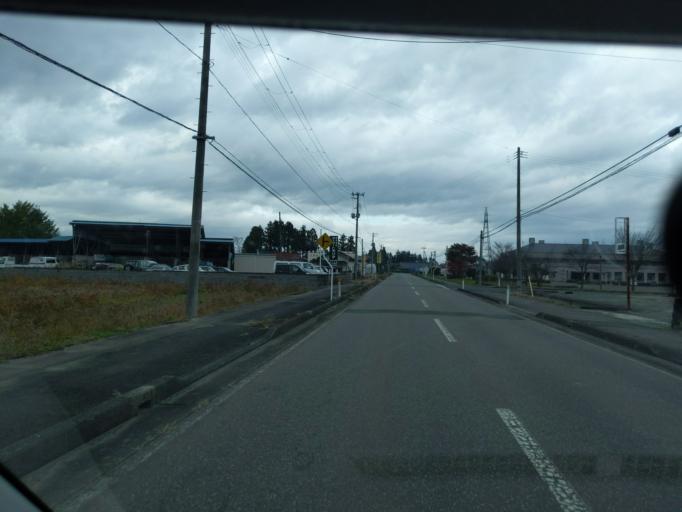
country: JP
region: Iwate
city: Mizusawa
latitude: 39.1271
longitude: 141.0673
